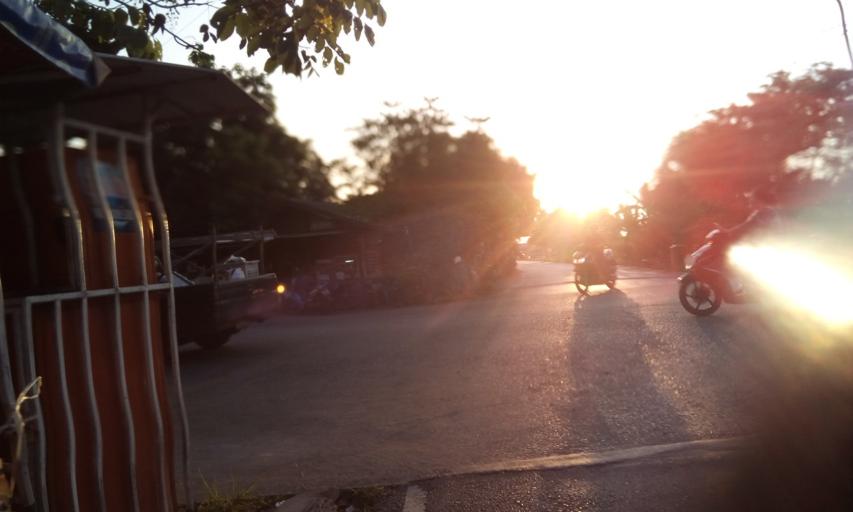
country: TH
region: Pathum Thani
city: Ban Rangsit
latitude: 14.0427
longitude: 100.7973
